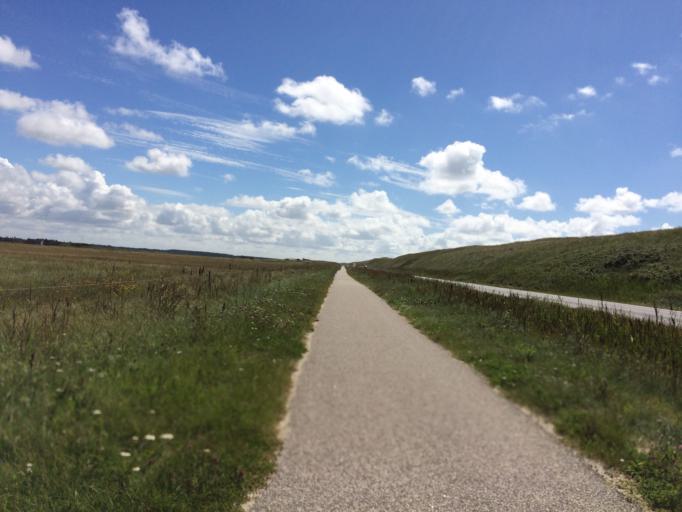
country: DK
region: Central Jutland
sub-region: Holstebro Kommune
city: Ulfborg
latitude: 56.3460
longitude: 8.1227
